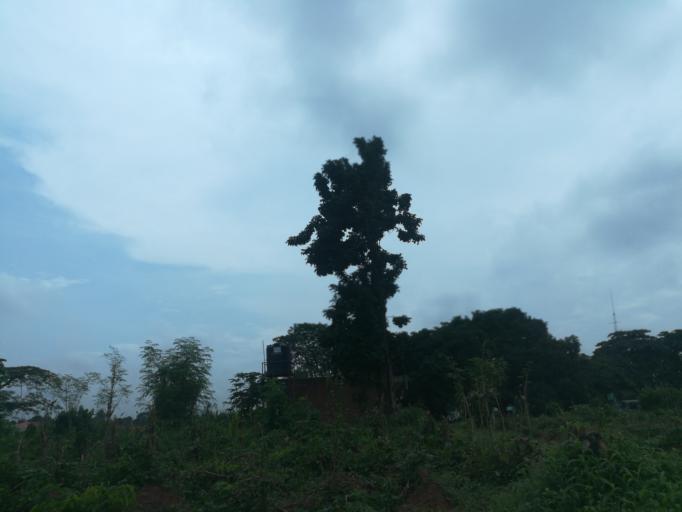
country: NG
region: Lagos
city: Oshodi
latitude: 6.5660
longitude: 3.3576
